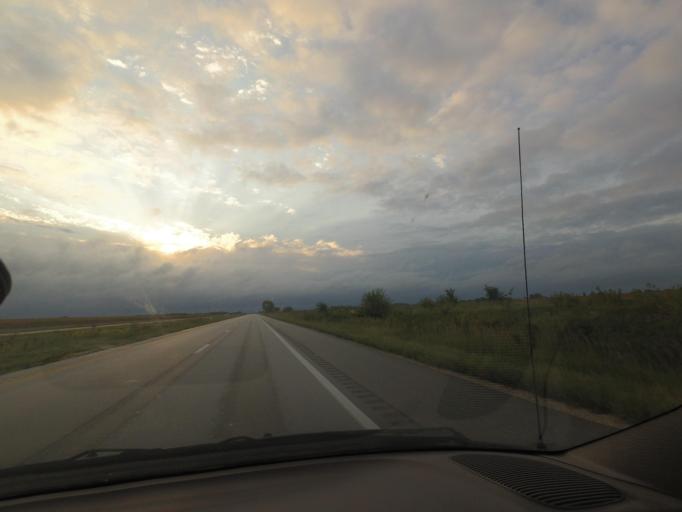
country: US
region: Missouri
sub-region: Shelby County
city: Shelbina
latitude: 39.6849
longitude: -92.0026
